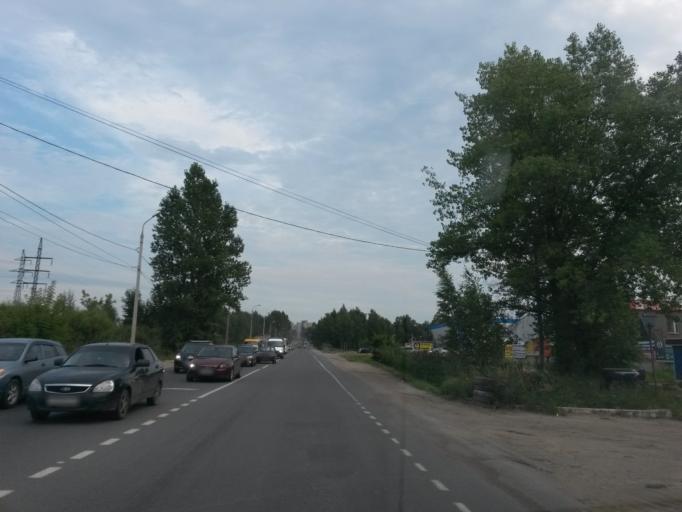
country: RU
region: Jaroslavl
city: Yaroslavl
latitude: 57.5943
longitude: 39.8128
